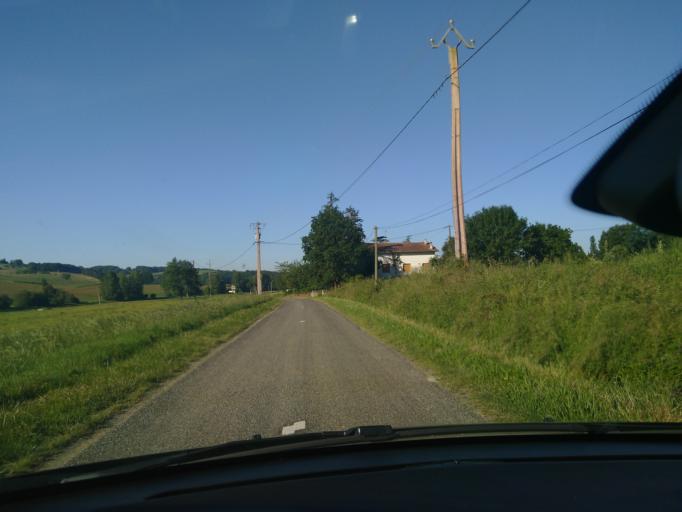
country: FR
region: Midi-Pyrenees
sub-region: Departement du Tarn-et-Garonne
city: Beaumont-de-Lomagne
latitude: 43.8128
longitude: 1.0379
